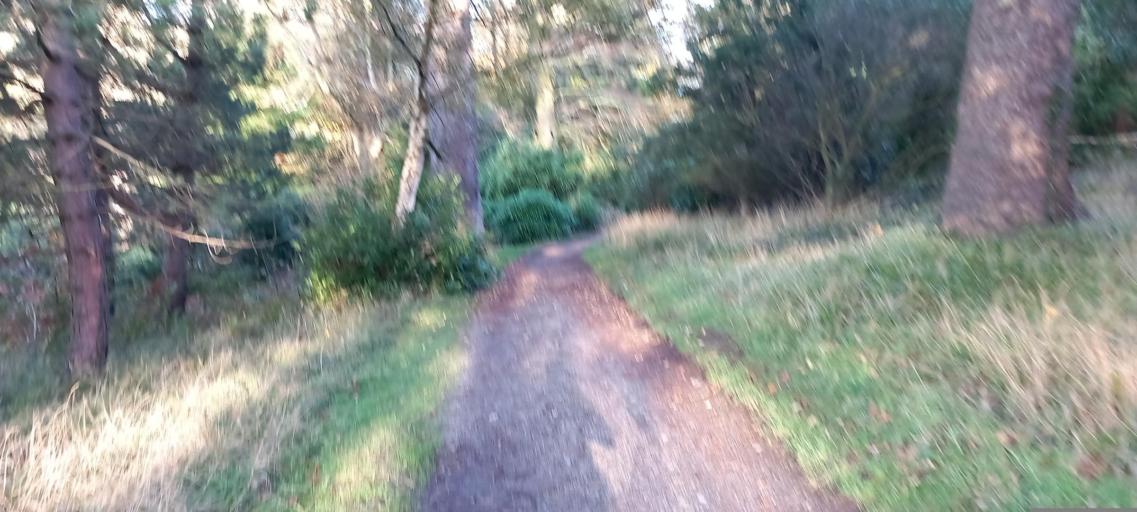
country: GB
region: Wales
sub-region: Gwynedd
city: Bangor
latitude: 53.2246
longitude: -4.0967
